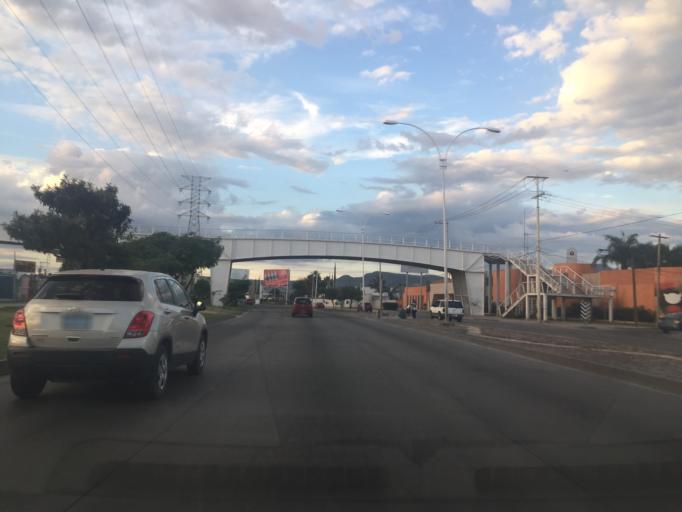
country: MX
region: Guanajuato
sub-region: Leon
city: Fraccionamiento Paraiso Real
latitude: 21.1044
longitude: -101.6232
